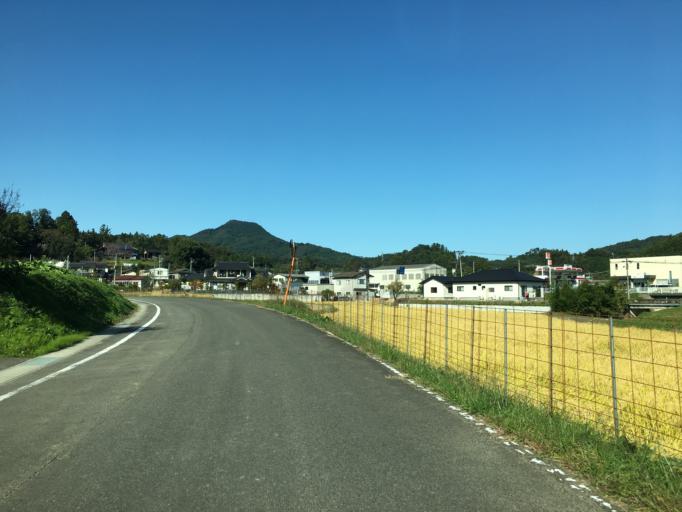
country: JP
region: Fukushima
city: Fukushima-shi
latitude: 37.6802
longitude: 140.5638
